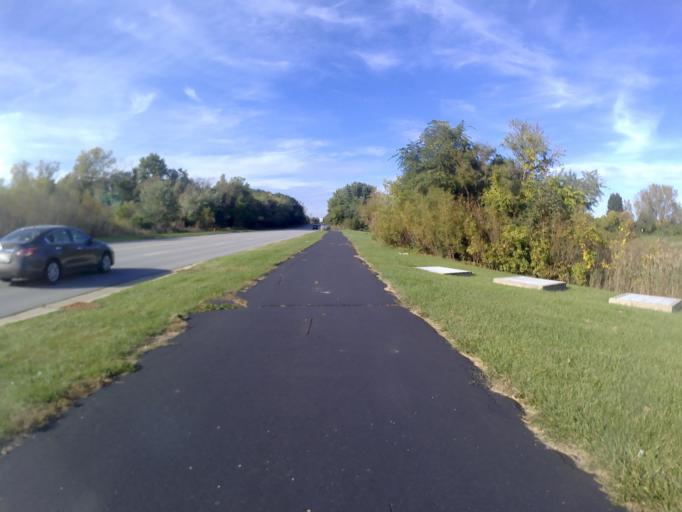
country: US
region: Illinois
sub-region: DuPage County
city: Woodridge
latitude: 41.7318
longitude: -88.0303
